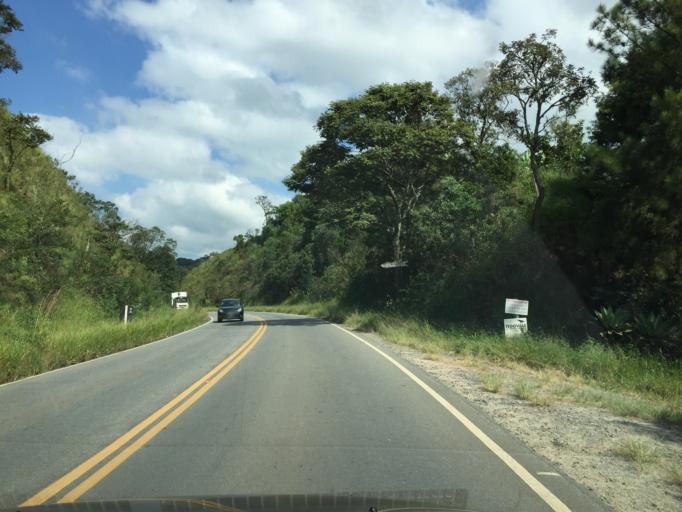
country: BR
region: Minas Gerais
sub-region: Passa Quatro
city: Passa Quatro
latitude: -22.3784
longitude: -44.9650
